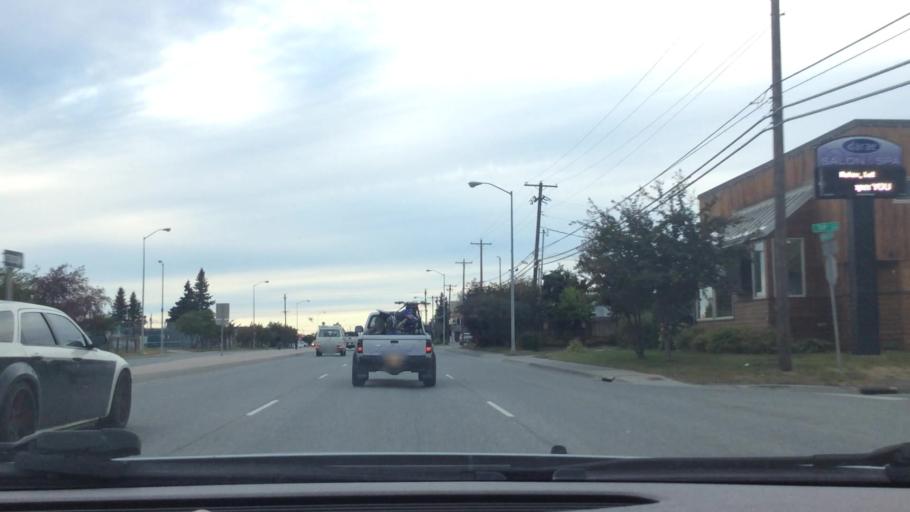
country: US
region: Alaska
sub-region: Anchorage Municipality
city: Anchorage
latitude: 61.1893
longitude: -149.9129
